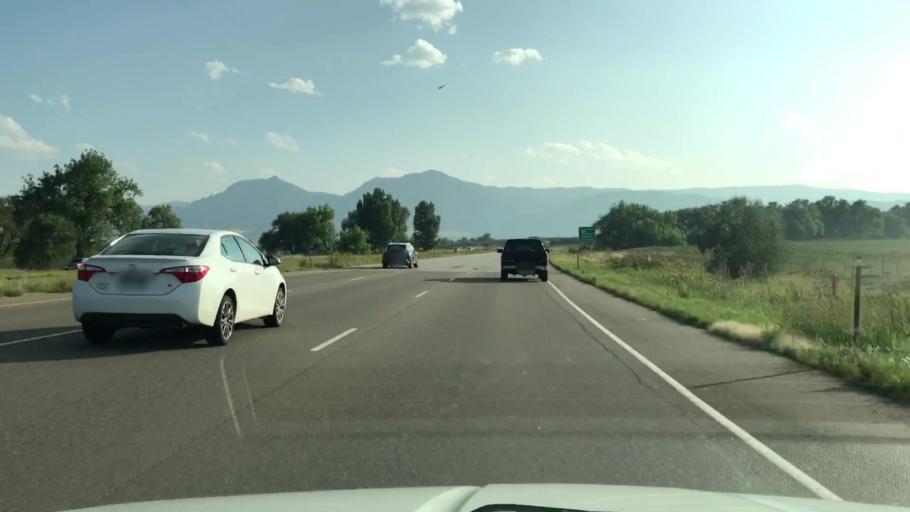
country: US
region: Colorado
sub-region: Boulder County
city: Boulder
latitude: 40.0478
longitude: -105.2379
